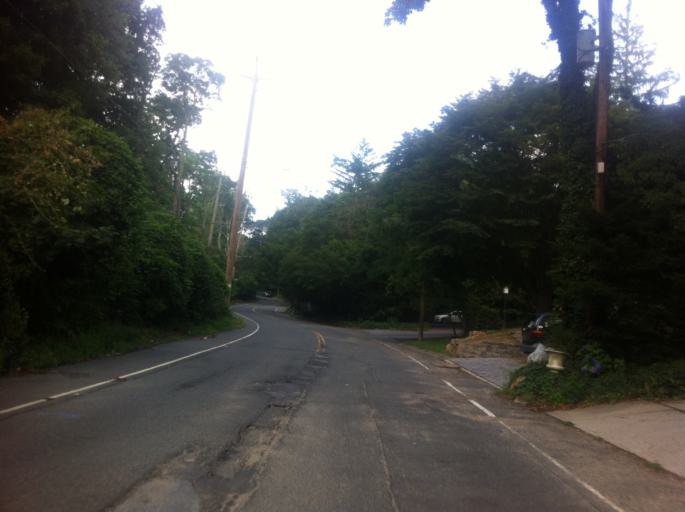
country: US
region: New York
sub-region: Nassau County
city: Glenwood Landing
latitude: 40.8310
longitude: -73.6482
